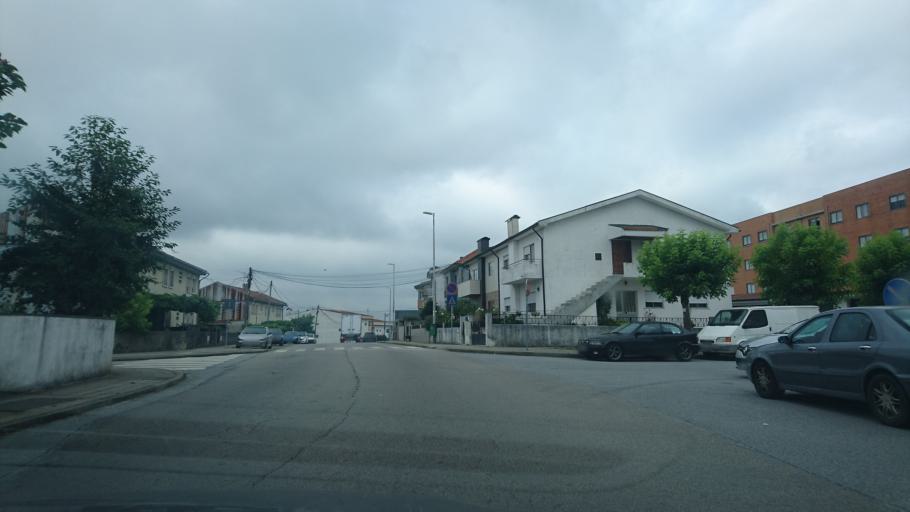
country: PT
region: Porto
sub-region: Valongo
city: Valongo
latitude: 41.1936
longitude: -8.5101
